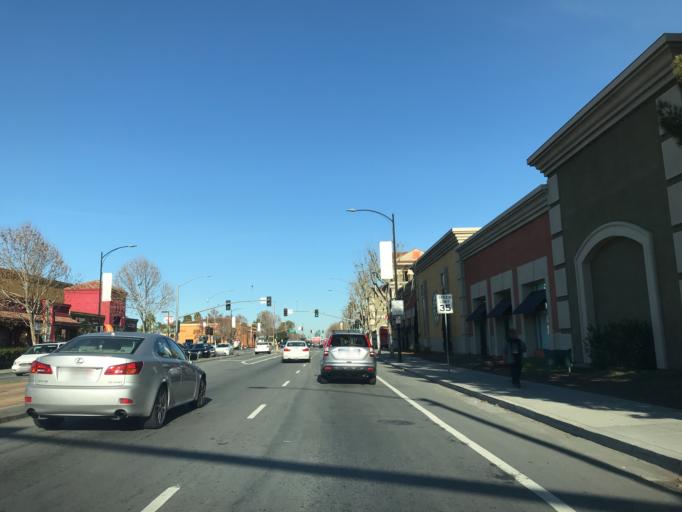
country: US
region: California
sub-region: Santa Clara County
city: Alum Rock
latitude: 37.3382
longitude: -121.8414
